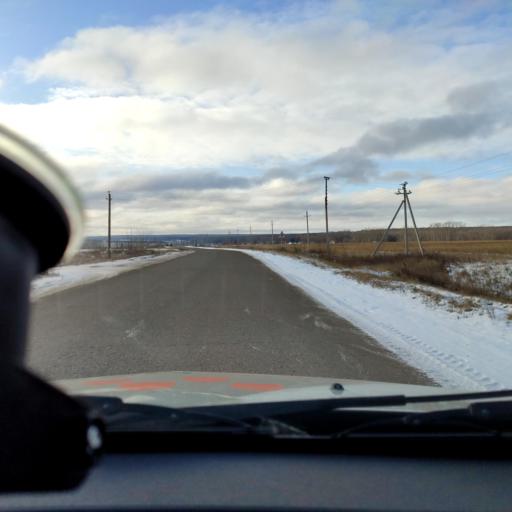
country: RU
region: Bashkortostan
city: Mikhaylovka
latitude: 54.8108
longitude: 55.7853
